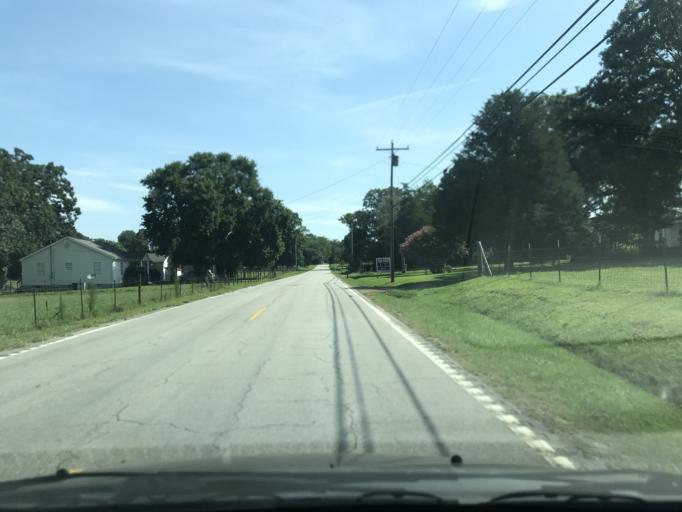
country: US
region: Tennessee
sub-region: Hamilton County
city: Lakesite
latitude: 35.2644
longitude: -85.0624
